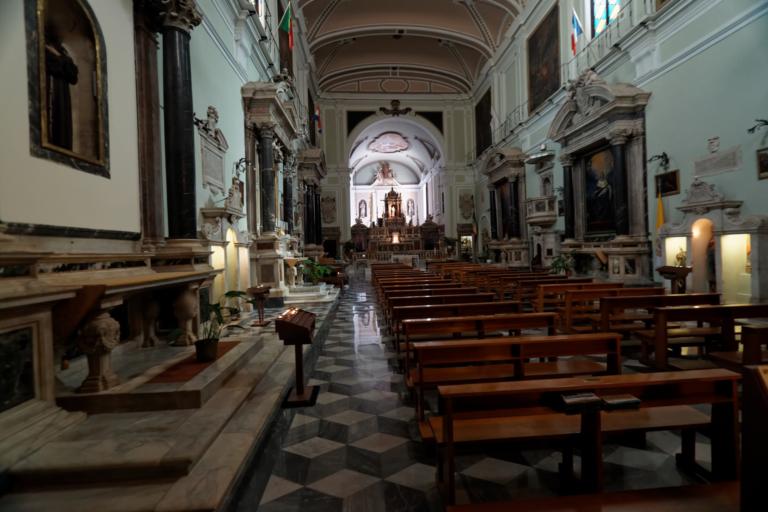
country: IT
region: Tuscany
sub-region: Provincia di Livorno
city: Livorno
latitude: 43.5521
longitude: 10.3101
